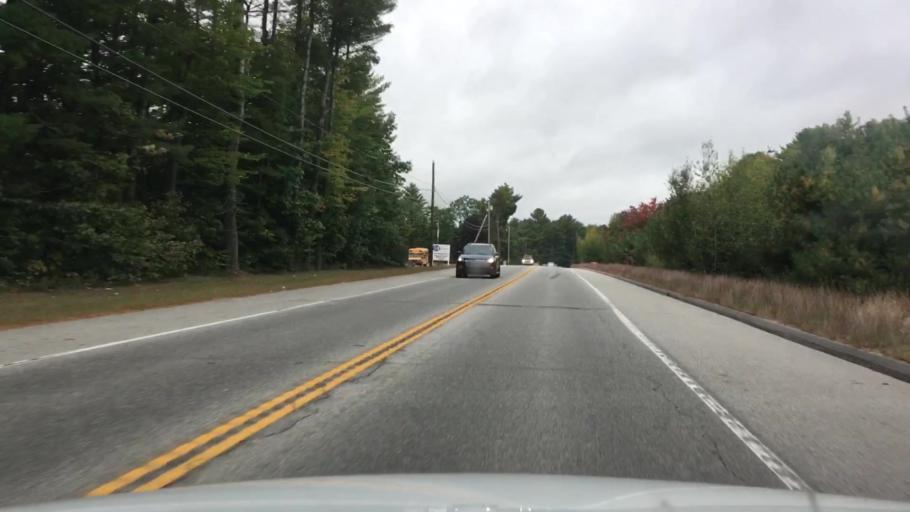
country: US
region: Maine
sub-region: Oxford County
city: Oxford
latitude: 44.1666
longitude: -70.5029
